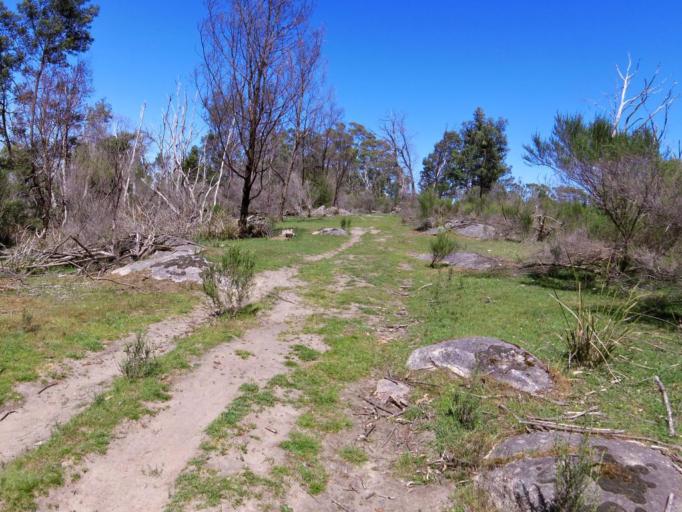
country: AU
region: Victoria
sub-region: Casey
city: Endeavour Hills
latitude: -37.9468
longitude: 145.2670
